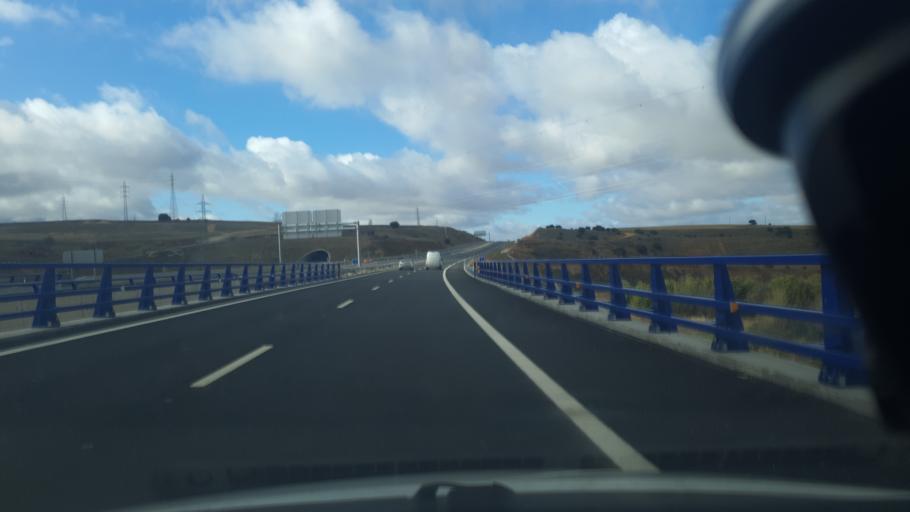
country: ES
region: Castille and Leon
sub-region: Provincia de Segovia
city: Segovia
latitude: 40.9187
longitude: -4.1225
